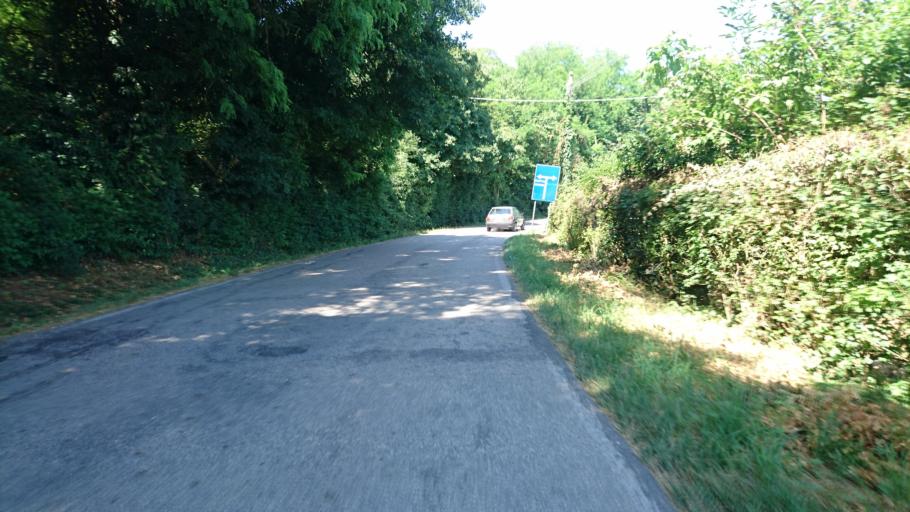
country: IT
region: Veneto
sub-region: Provincia di Padova
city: Bastia
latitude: 45.3922
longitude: 11.6768
